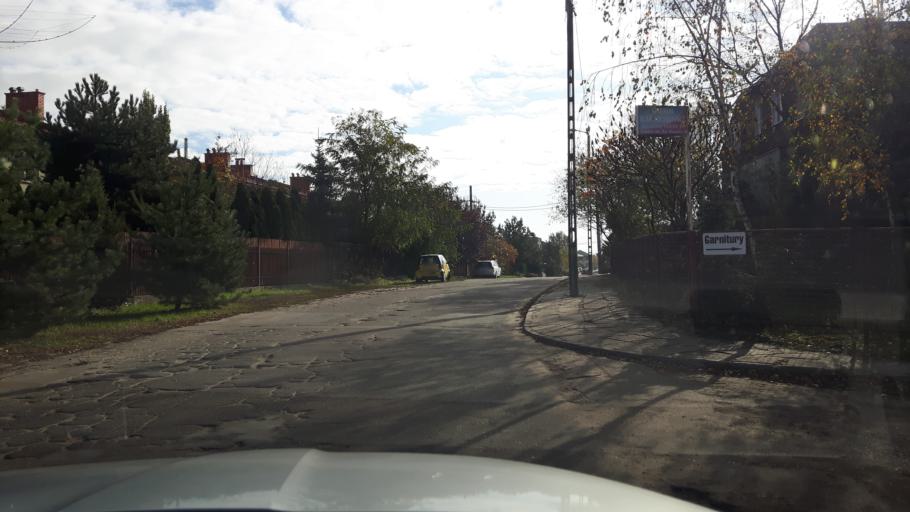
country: PL
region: Masovian Voivodeship
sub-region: Powiat wolominski
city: Zabki
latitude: 52.3011
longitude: 21.0978
